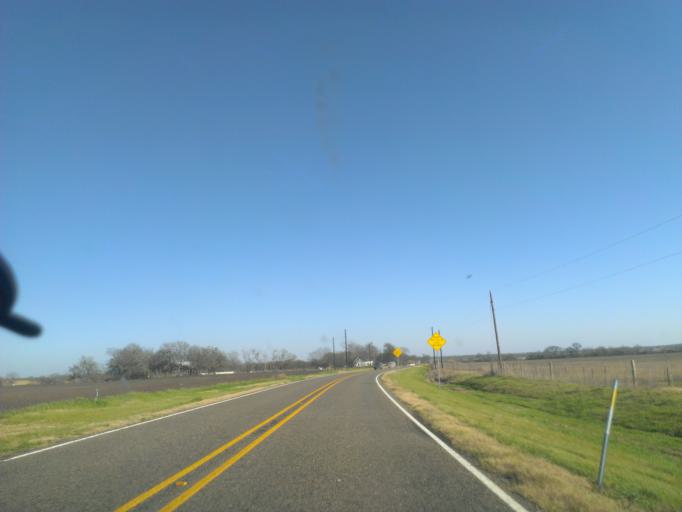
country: US
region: Texas
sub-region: Milam County
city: Thorndale
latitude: 30.5400
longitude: -97.2657
